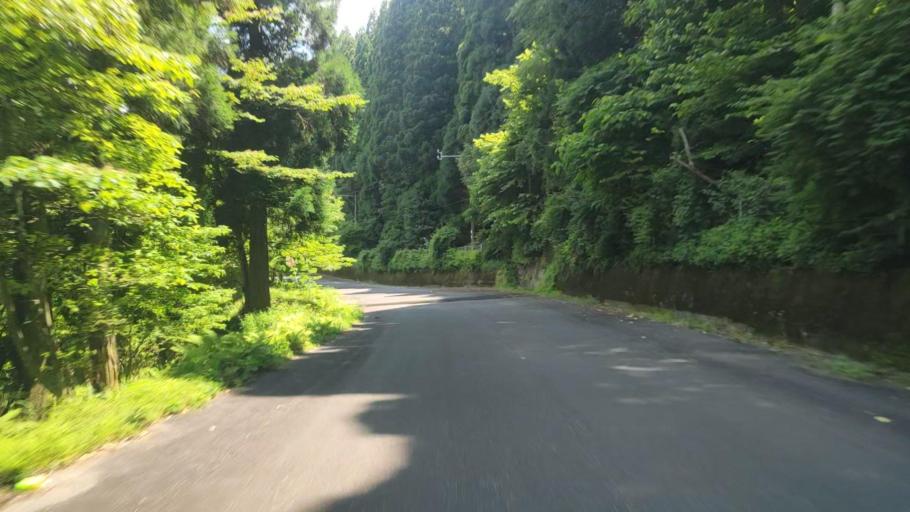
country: JP
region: Fukui
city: Ono
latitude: 35.7283
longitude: 136.5782
